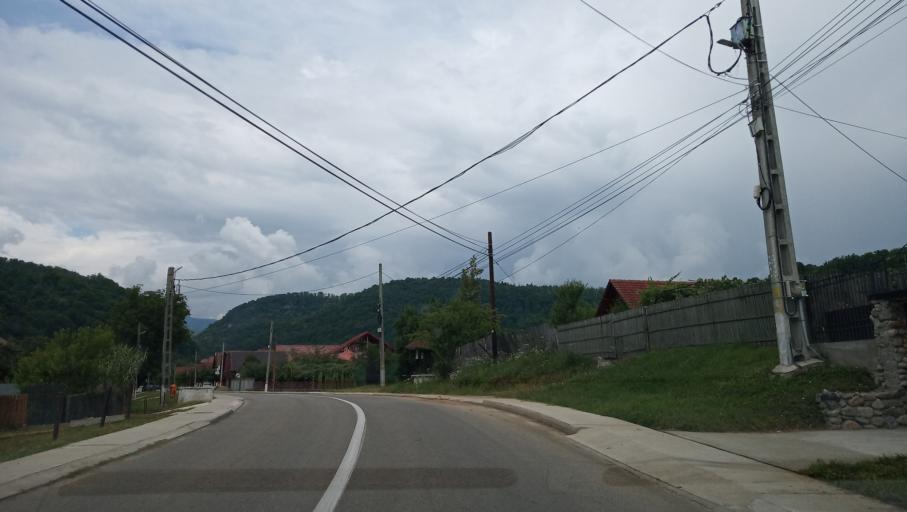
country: RO
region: Gorj
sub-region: Comuna Tismana
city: Tismana
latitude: 45.0614
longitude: 22.9444
